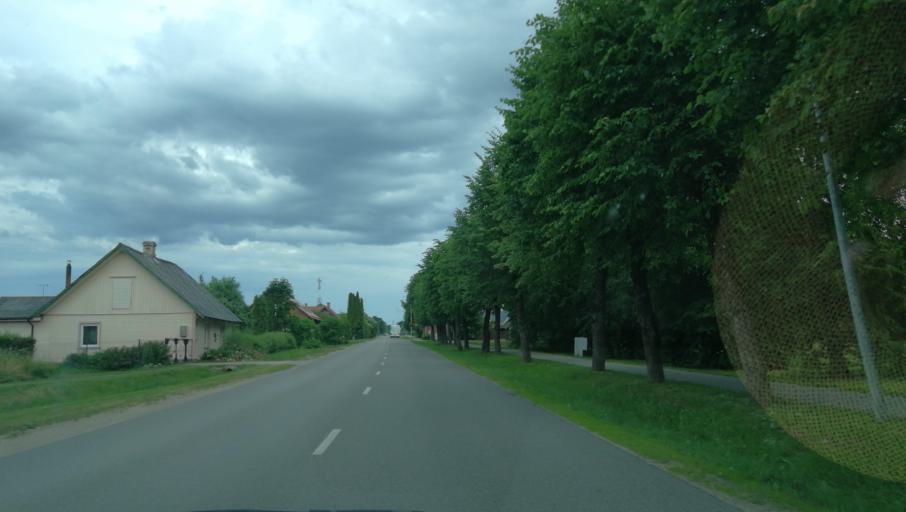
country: LV
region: Rujienas
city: Rujiena
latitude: 57.8903
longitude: 25.3476
